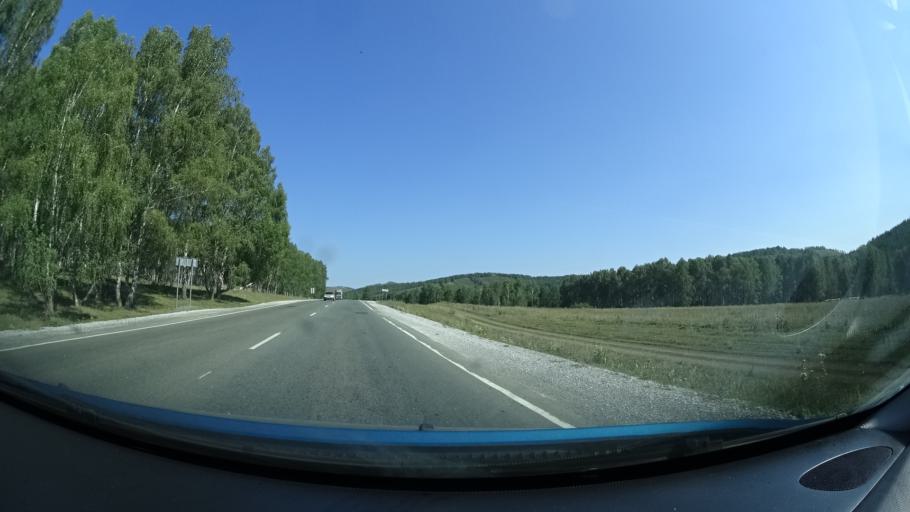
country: RU
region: Bashkortostan
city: Abzakovo
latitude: 53.8424
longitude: 58.5819
